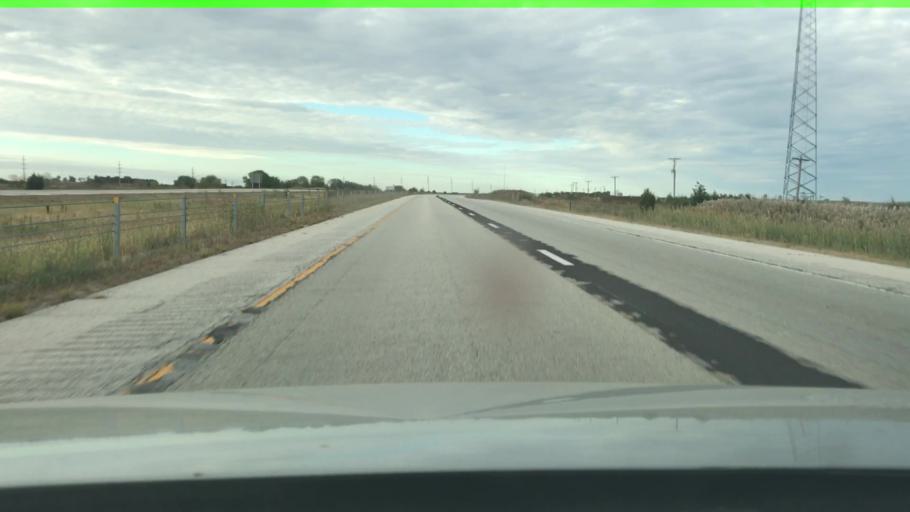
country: US
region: Illinois
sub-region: Livingston County
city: Odell
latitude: 40.9898
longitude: -88.5416
